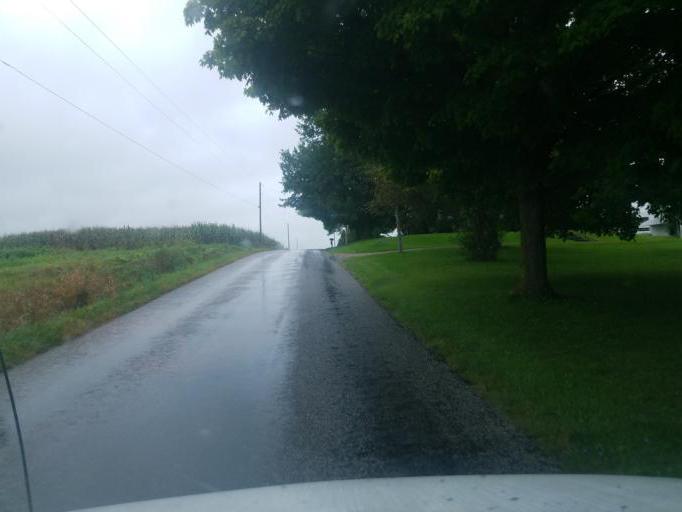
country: US
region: Ohio
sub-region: Medina County
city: Lodi
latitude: 40.9747
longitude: -82.0074
